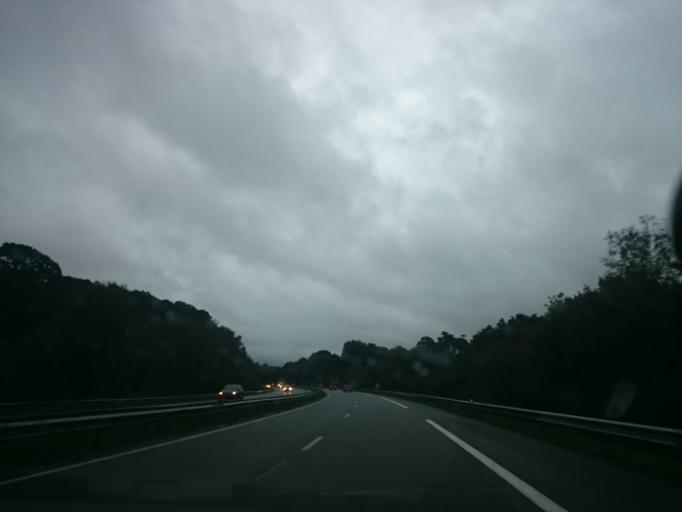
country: FR
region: Brittany
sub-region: Departement du Finistere
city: Dineault
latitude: 48.2537
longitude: -4.1149
